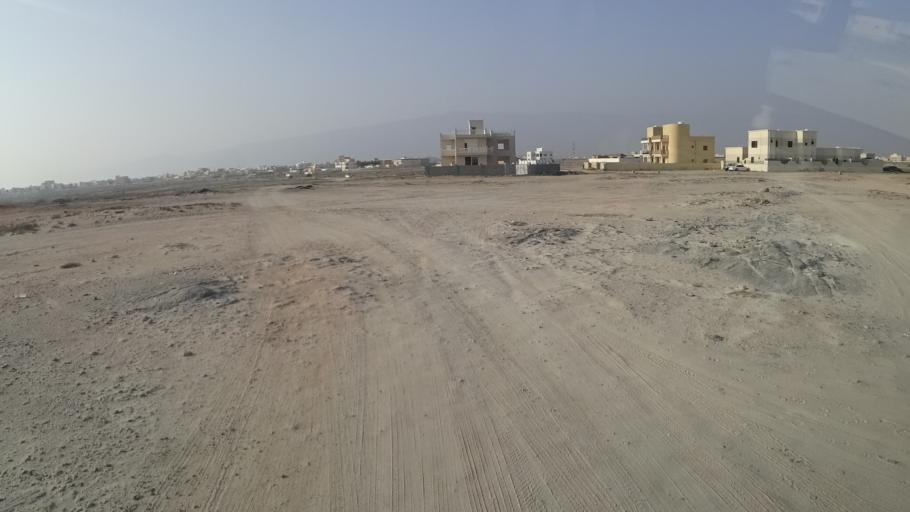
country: OM
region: Zufar
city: Salalah
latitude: 16.9726
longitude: 54.7015
